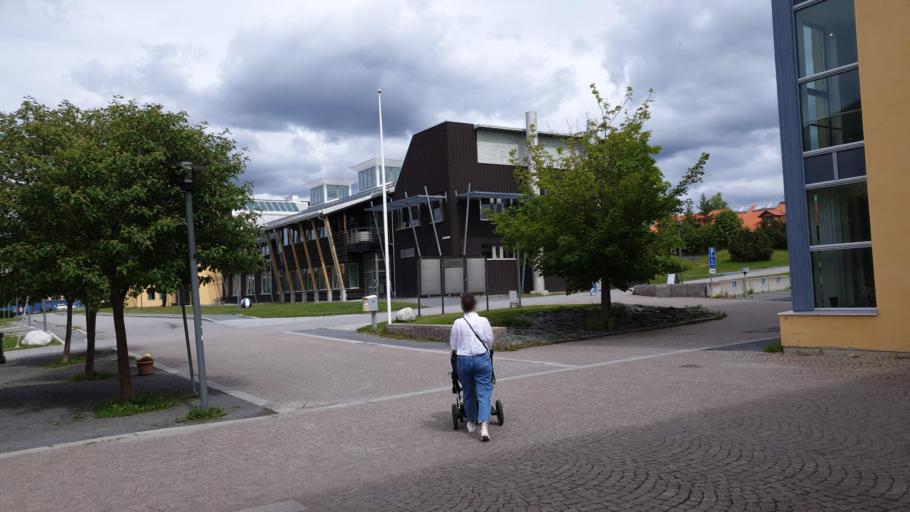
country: SE
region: Jaemtland
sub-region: OEstersunds Kommun
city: Ostersund
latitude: 63.1769
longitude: 14.6489
